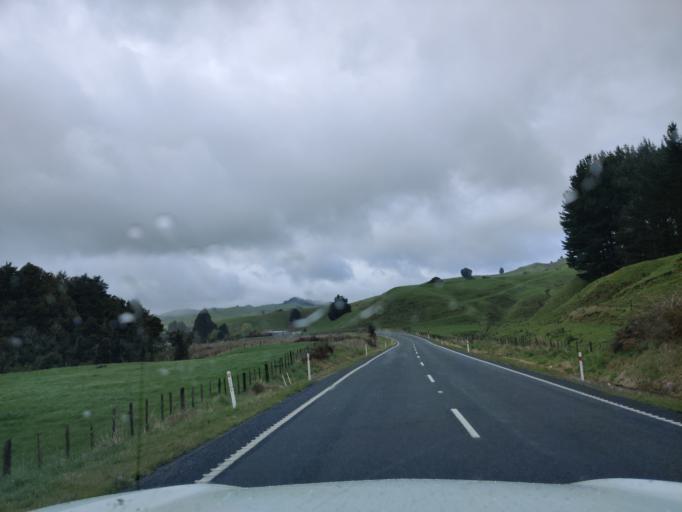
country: NZ
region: Waikato
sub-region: Otorohanga District
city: Otorohanga
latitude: -38.6915
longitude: 175.2141
